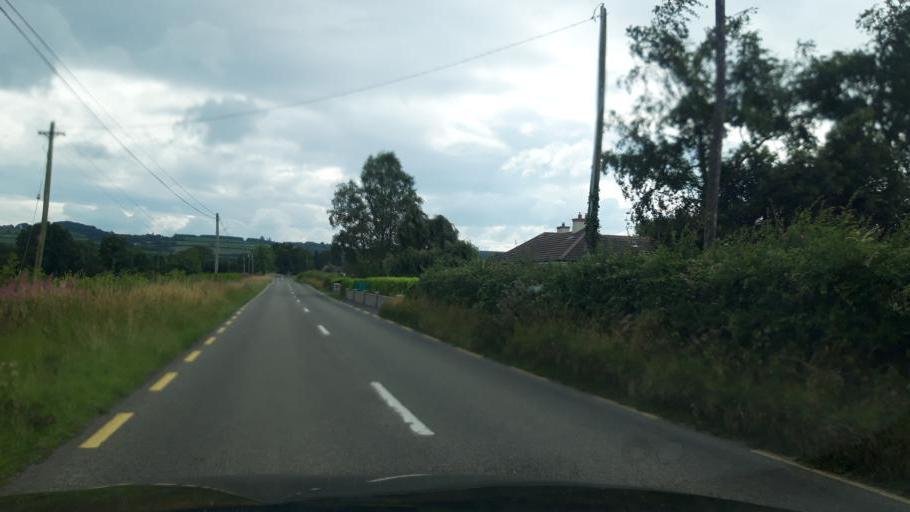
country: IE
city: Ballylinan
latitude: 52.9129
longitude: -7.0760
